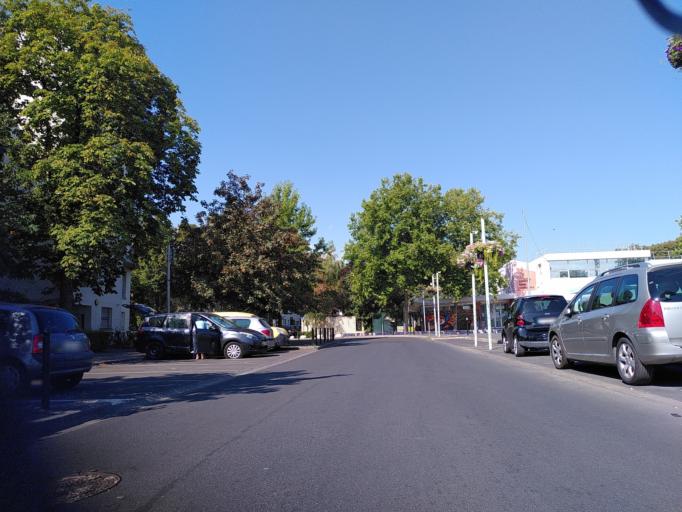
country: FR
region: Ile-de-France
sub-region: Departement de l'Essonne
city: Paray-Vieille-Poste
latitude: 48.7033
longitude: 2.3630
